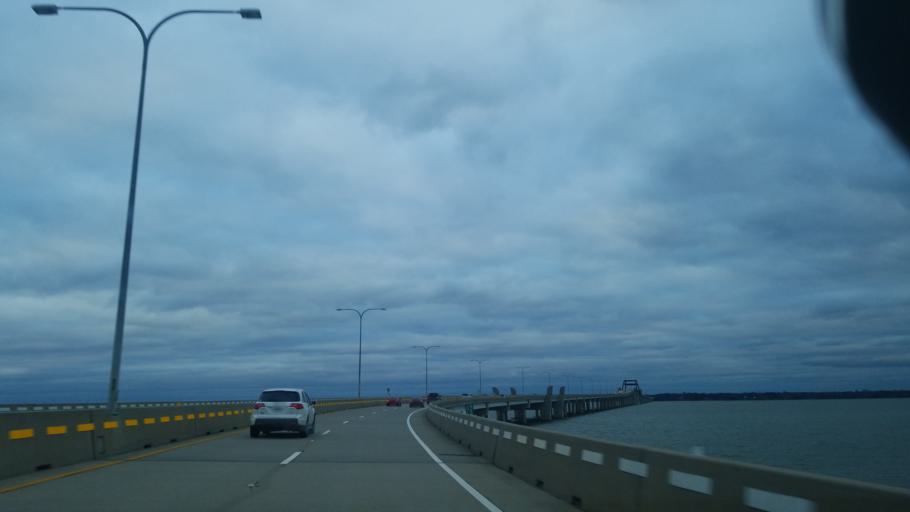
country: US
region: Texas
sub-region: Denton County
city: Lake Dallas
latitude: 33.1383
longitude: -97.0159
